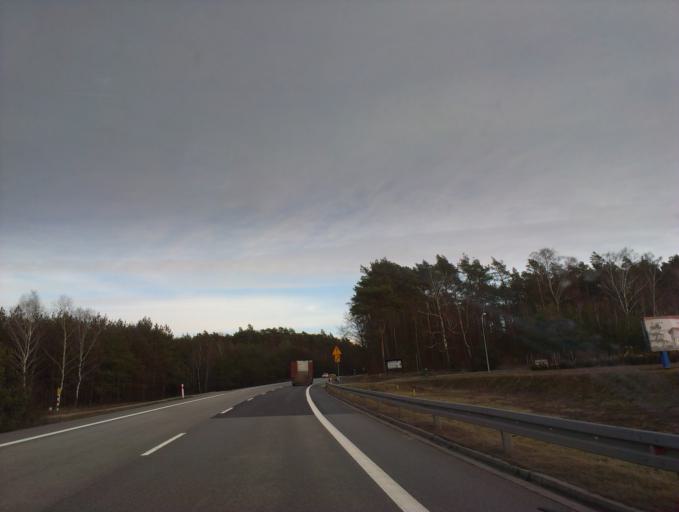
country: PL
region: Kujawsko-Pomorskie
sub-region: Powiat lipnowski
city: Skepe
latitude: 52.8779
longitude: 19.3332
